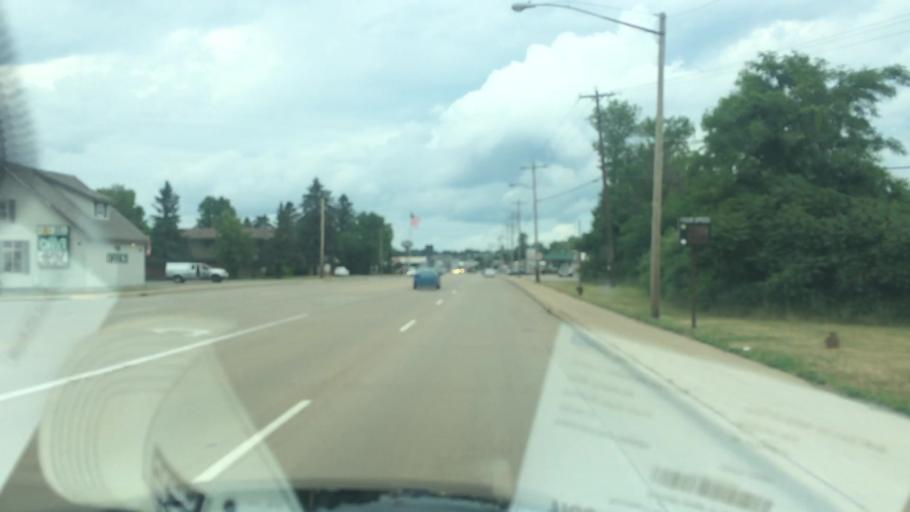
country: US
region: Wisconsin
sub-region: Marathon County
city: Schofield
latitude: 44.9226
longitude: -89.6130
